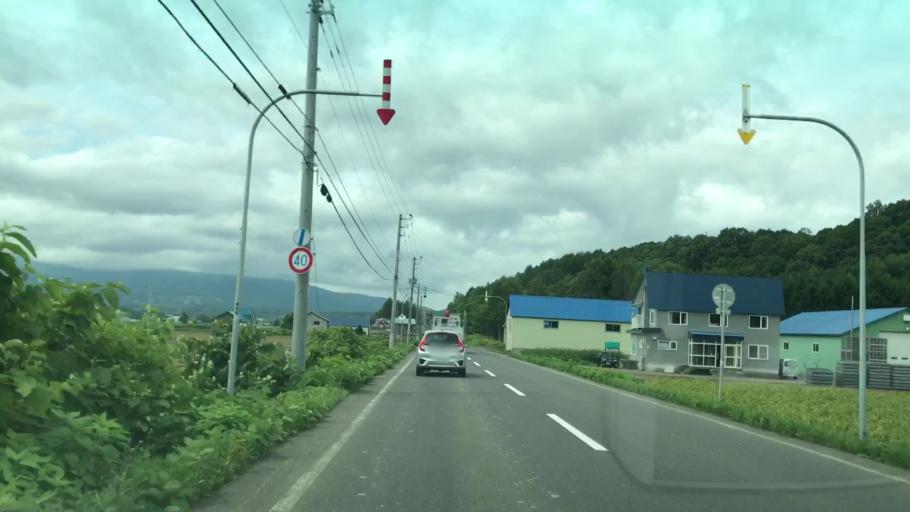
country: JP
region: Hokkaido
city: Niseko Town
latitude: 42.9318
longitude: 140.8002
